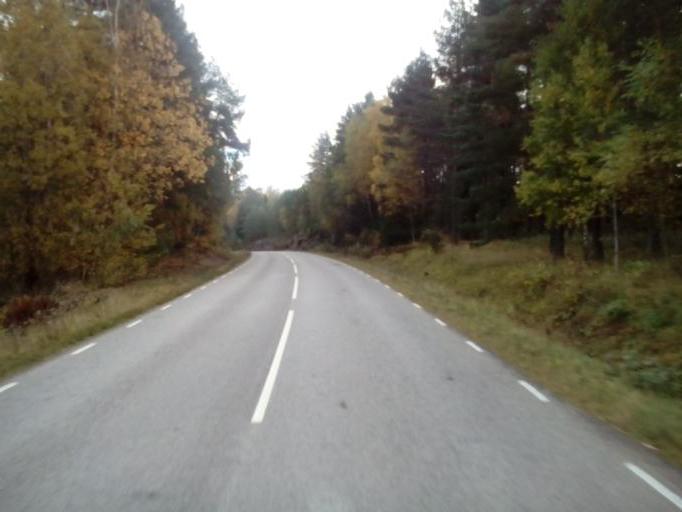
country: SE
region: Kalmar
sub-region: Vasterviks Kommun
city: Gamleby
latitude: 57.8865
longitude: 16.3475
